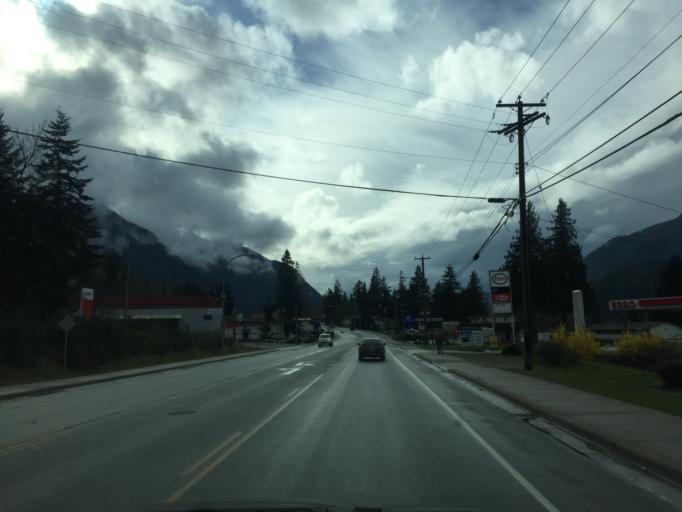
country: CA
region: British Columbia
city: Hope
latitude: 49.3754
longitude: -121.4337
